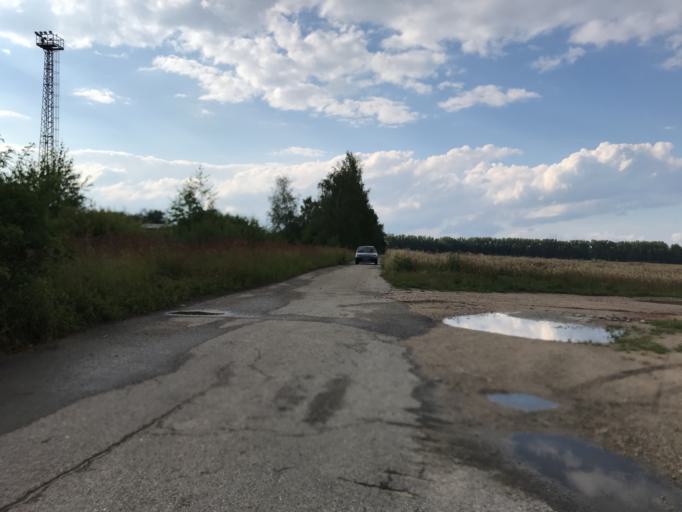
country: CZ
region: Jihocesky
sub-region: Okres Jindrichuv Hradec
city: Trebon
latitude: 49.0192
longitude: 14.7600
